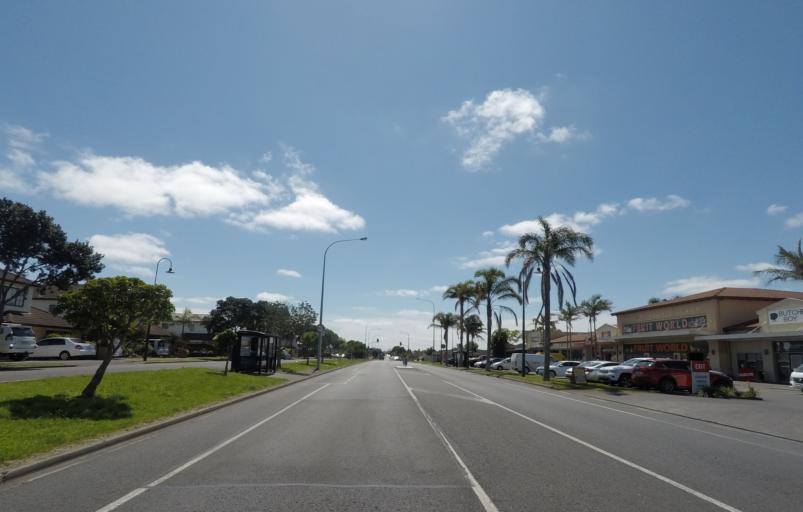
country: NZ
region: Auckland
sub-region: Auckland
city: Manukau City
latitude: -36.9500
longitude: 174.9106
